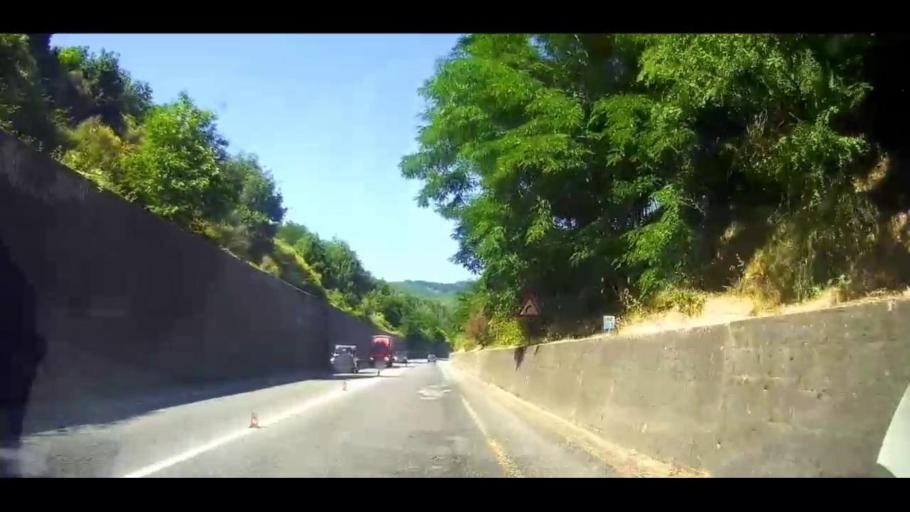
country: IT
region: Calabria
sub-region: Provincia di Cosenza
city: Celico
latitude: 39.3123
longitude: 16.3288
